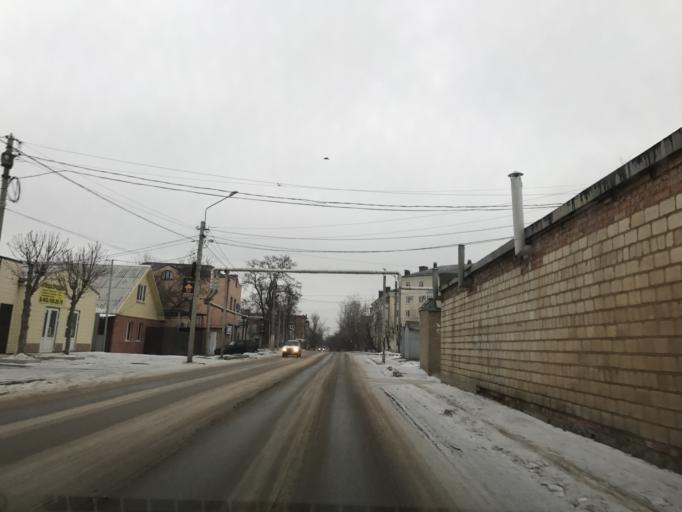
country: RU
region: Rostov
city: Kamensk-Shakhtinskiy
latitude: 48.3179
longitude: 40.2595
